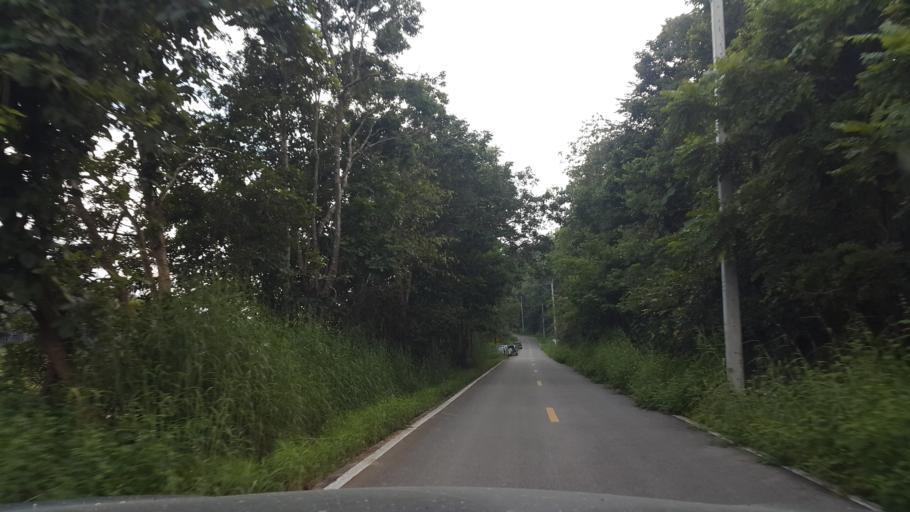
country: TH
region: Chiang Mai
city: San Sai
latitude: 18.9442
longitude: 99.0636
